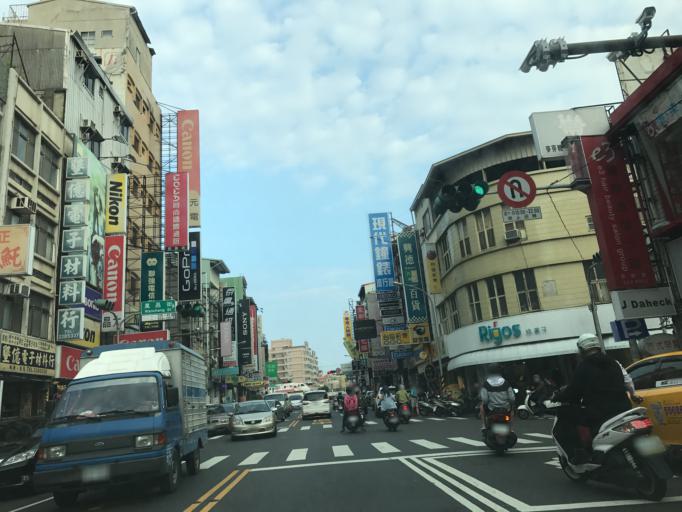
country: TW
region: Taiwan
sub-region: Tainan
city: Tainan
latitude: 22.9945
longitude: 120.2106
